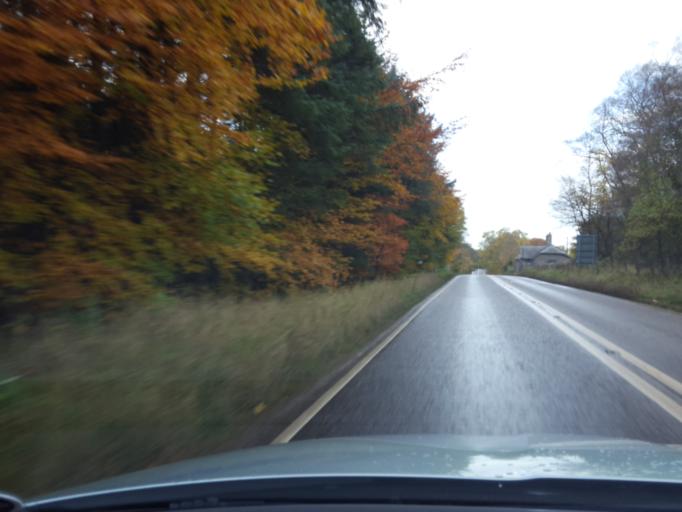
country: GB
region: Scotland
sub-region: South Lanarkshire
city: Carnwath
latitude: 55.7104
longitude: -3.5991
